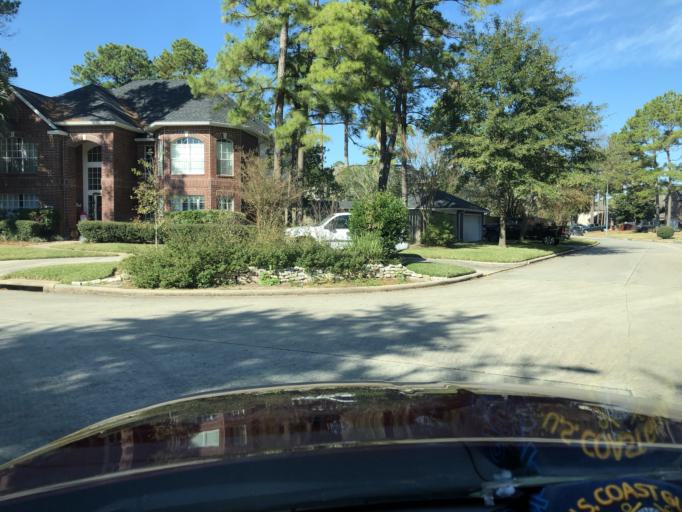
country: US
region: Texas
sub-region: Harris County
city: Tomball
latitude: 30.0211
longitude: -95.5519
